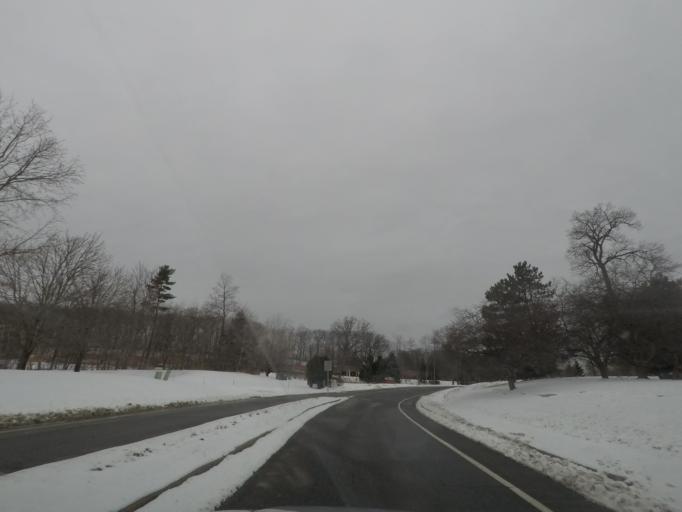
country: US
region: New York
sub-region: Schenectady County
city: Niskayuna
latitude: 42.7599
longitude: -73.8223
